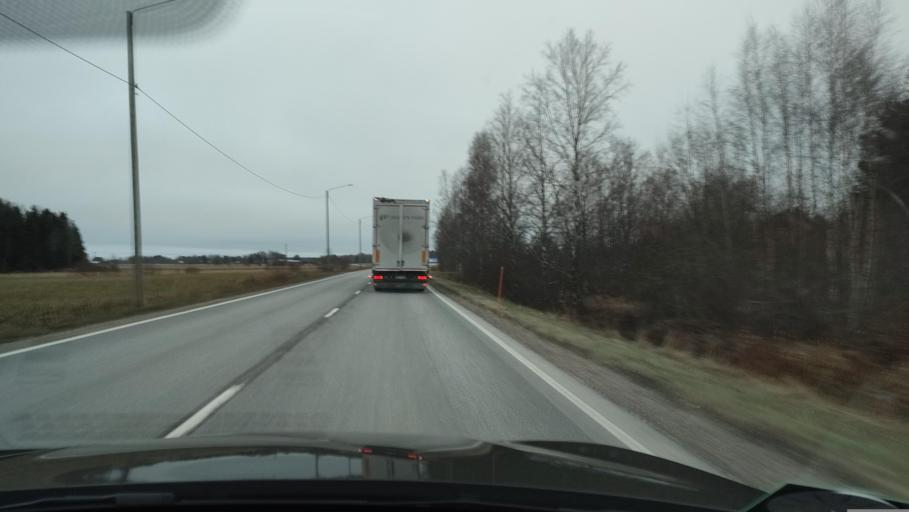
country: FI
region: Southern Ostrobothnia
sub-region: Suupohja
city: Kauhajoki
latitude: 62.3528
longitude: 22.0556
